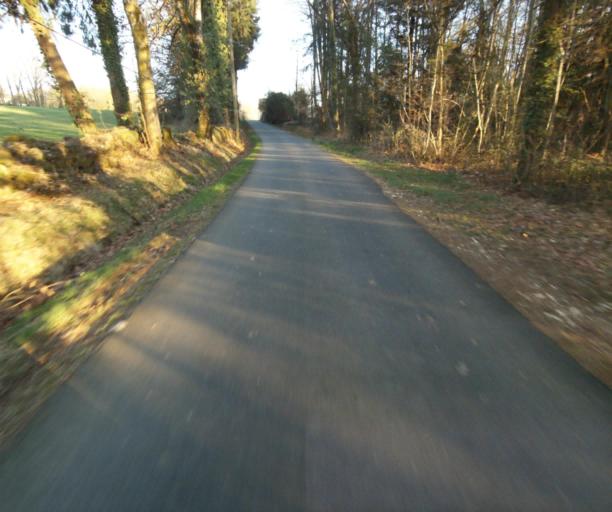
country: FR
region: Limousin
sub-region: Departement de la Correze
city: Seilhac
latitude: 45.3520
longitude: 1.7098
